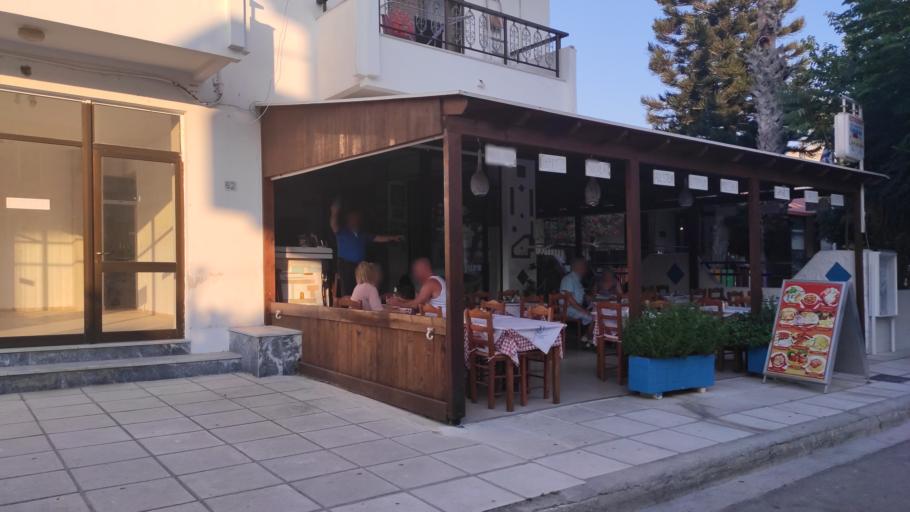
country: GR
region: South Aegean
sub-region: Nomos Dodekanisou
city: Kos
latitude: 36.9002
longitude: 27.2824
